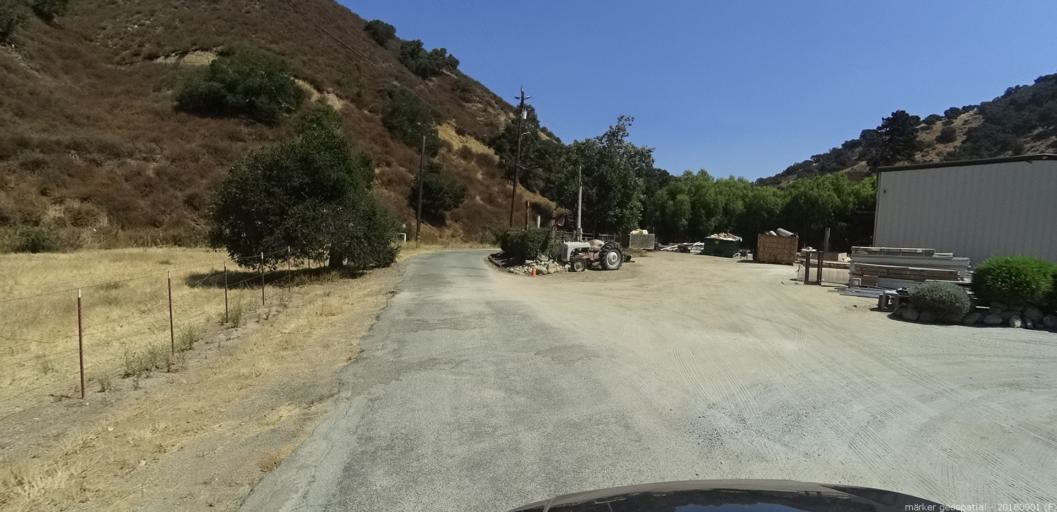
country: US
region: California
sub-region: Monterey County
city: Gonzales
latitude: 36.6046
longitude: -121.4003
